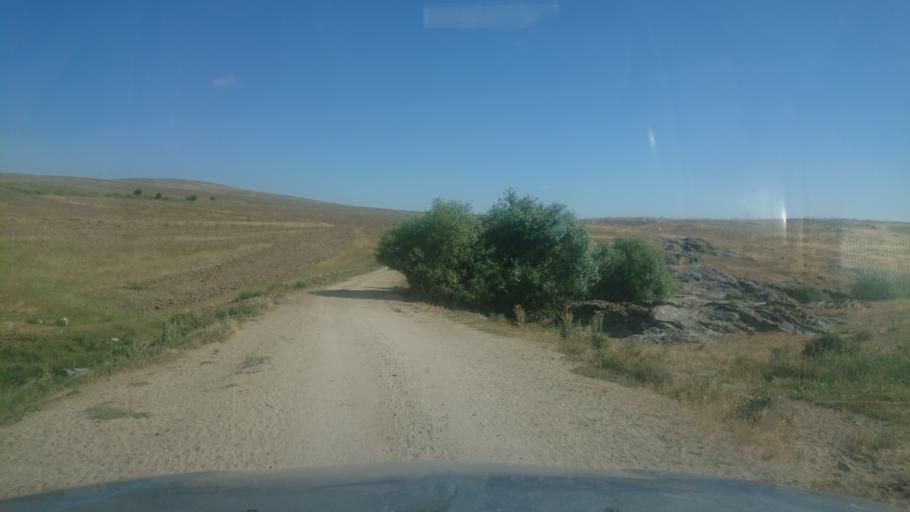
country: TR
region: Aksaray
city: Sariyahsi
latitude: 38.9130
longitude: 33.8553
